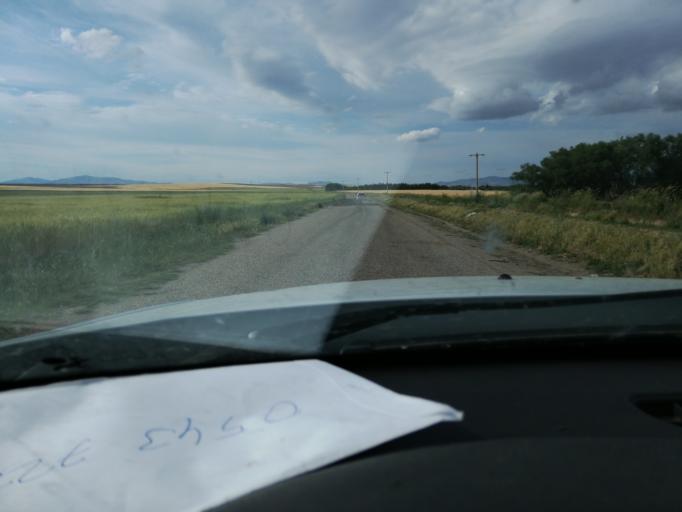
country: TR
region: Kirsehir
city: Kirsehir
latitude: 39.0092
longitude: 34.1200
